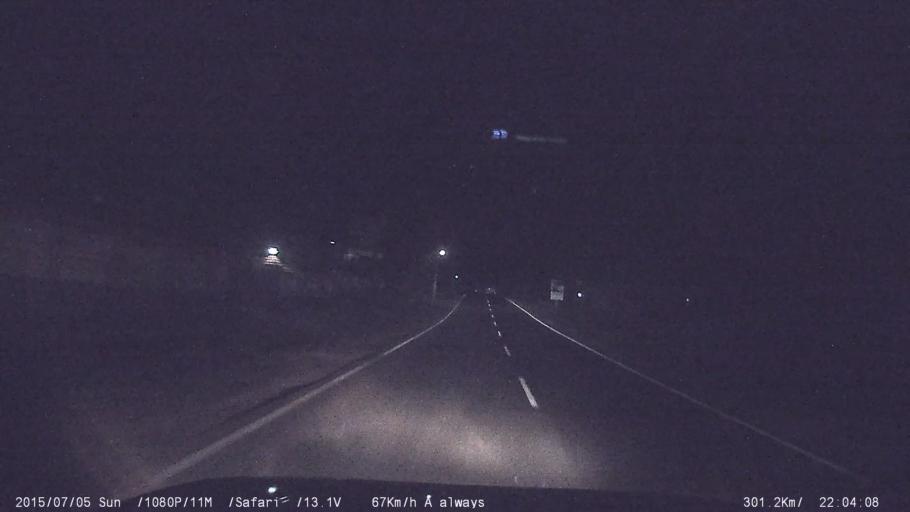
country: IN
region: Kerala
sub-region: Palakkad district
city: Mannarakkat
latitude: 10.9247
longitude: 76.5245
